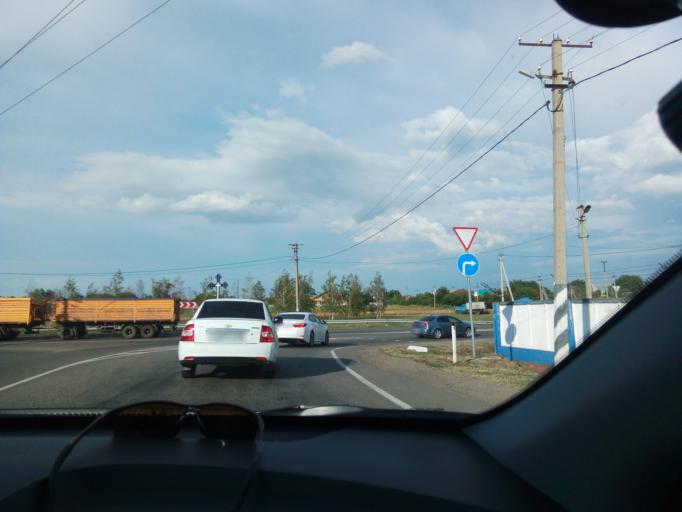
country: RU
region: Krasnodarskiy
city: Labinsk
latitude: 44.6661
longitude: 40.6971
